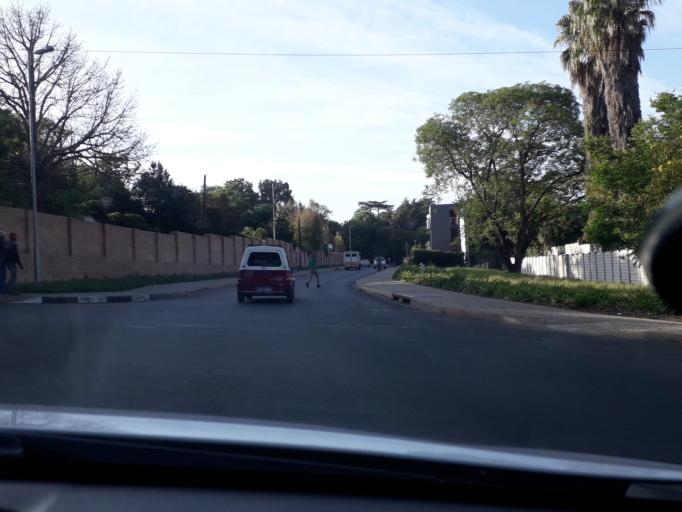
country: ZA
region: Gauteng
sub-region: City of Johannesburg Metropolitan Municipality
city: Johannesburg
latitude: -26.1255
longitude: 28.0731
